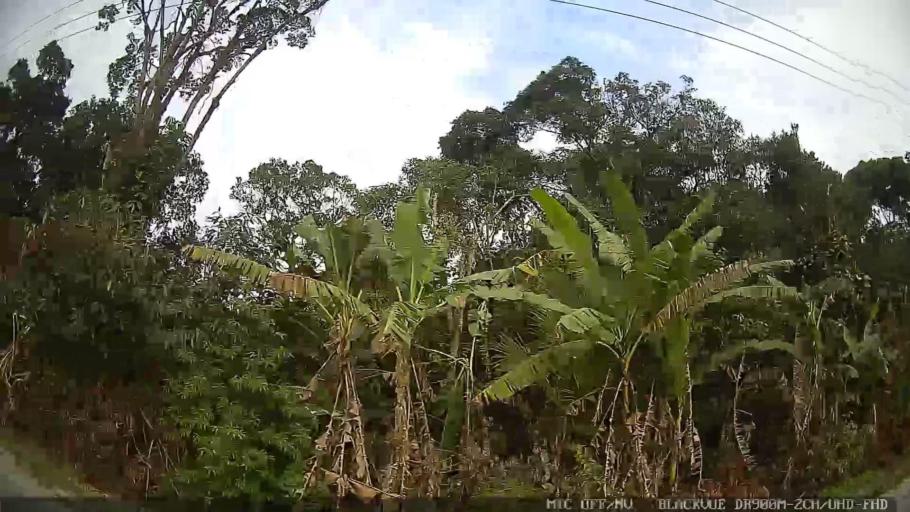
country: BR
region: Sao Paulo
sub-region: Guaruja
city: Guaruja
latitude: -23.9724
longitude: -46.2176
